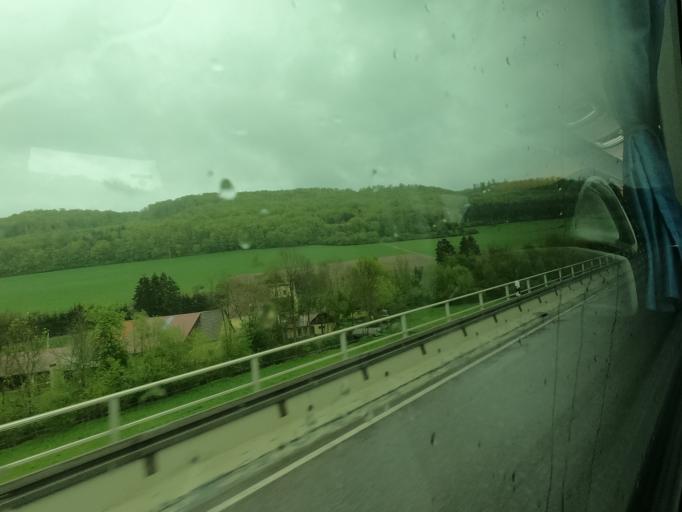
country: DE
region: Baden-Wuerttemberg
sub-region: Regierungsbezirk Stuttgart
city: Oberkochen
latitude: 48.7986
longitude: 10.1266
